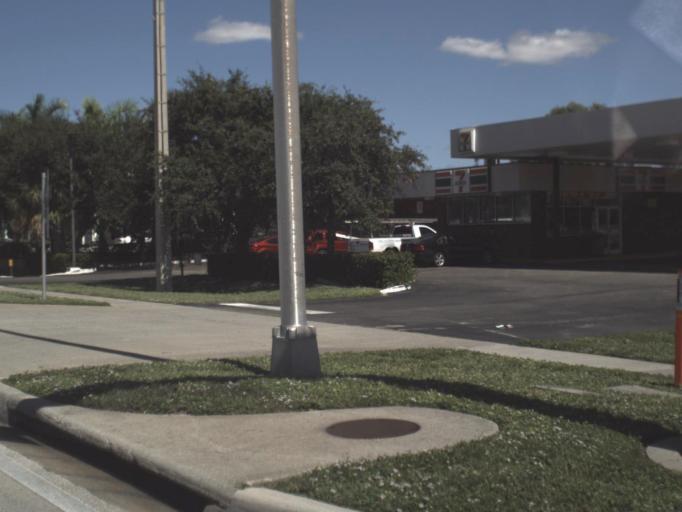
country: US
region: Florida
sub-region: Collier County
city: Pine Ridge
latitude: 26.2031
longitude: -81.8001
